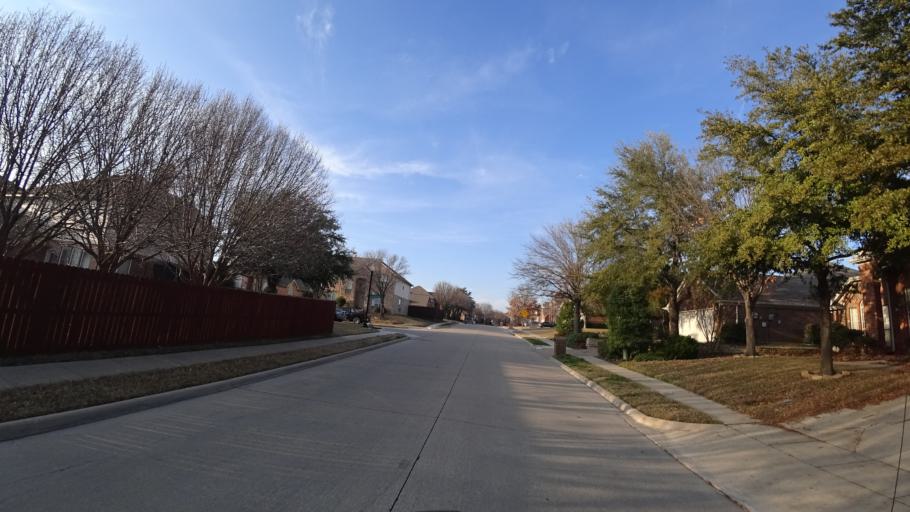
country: US
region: Texas
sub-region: Dallas County
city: Coppell
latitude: 32.9908
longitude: -96.9867
